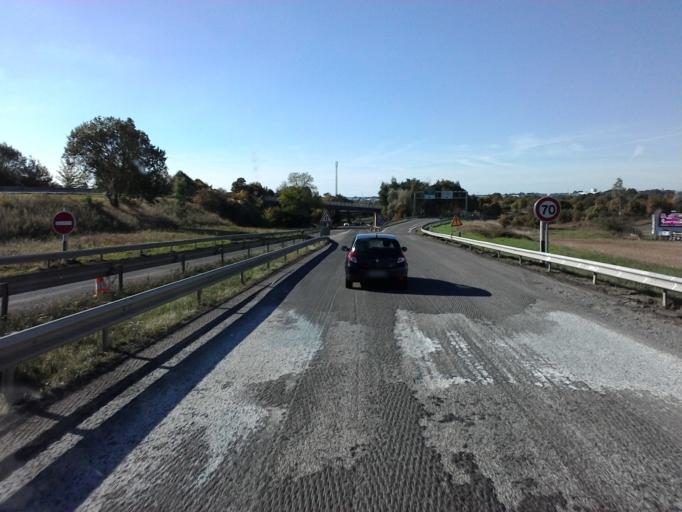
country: FR
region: Lorraine
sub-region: Departement de Meurthe-et-Moselle
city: Mexy
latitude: 49.5025
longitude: 5.7918
